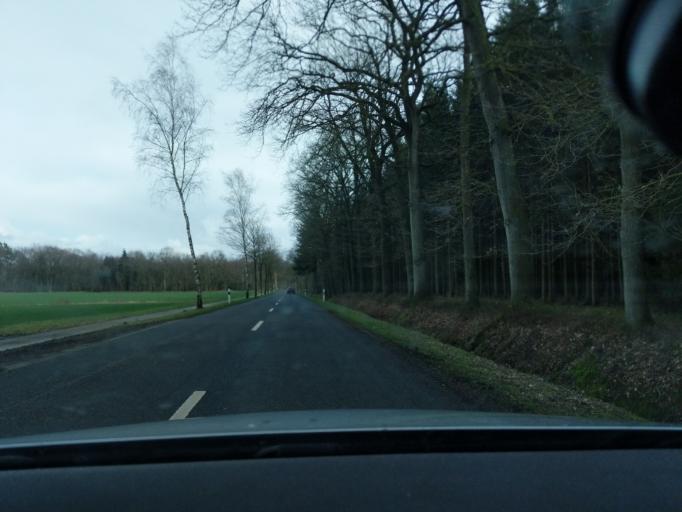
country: DE
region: Lower Saxony
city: Himmelpforten
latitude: 53.5823
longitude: 9.2874
